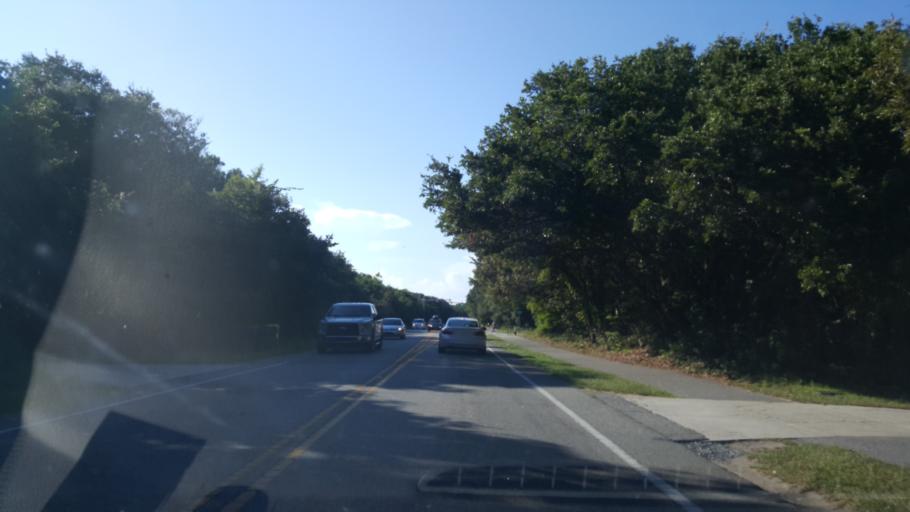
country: US
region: North Carolina
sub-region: Dare County
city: Southern Shores
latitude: 36.1427
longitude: -75.7386
